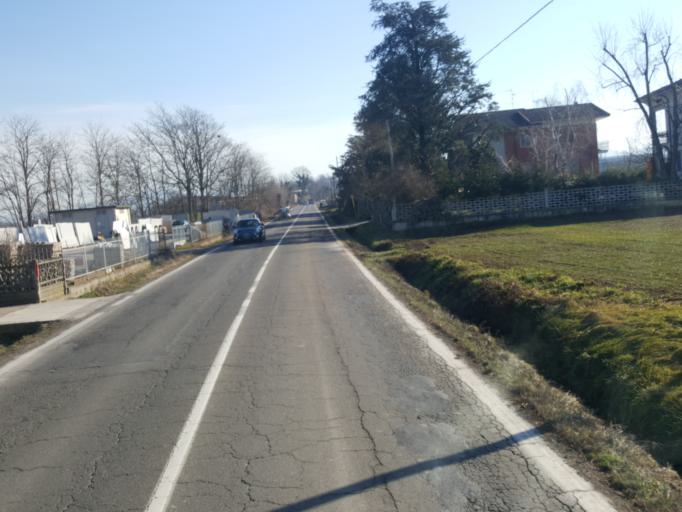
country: IT
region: Piedmont
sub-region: Provincia di Alessandria
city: Castellar Guidobono
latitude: 44.9061
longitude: 8.9346
